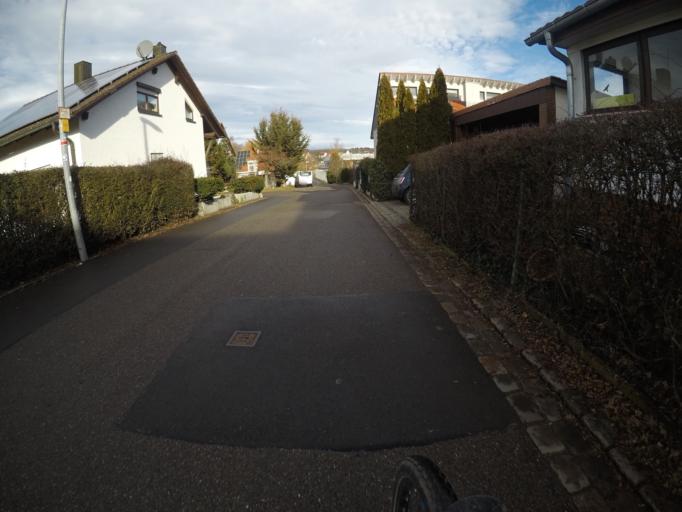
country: DE
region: Baden-Wuerttemberg
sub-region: Regierungsbezirk Stuttgart
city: Gartringen
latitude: 48.6443
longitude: 8.9016
